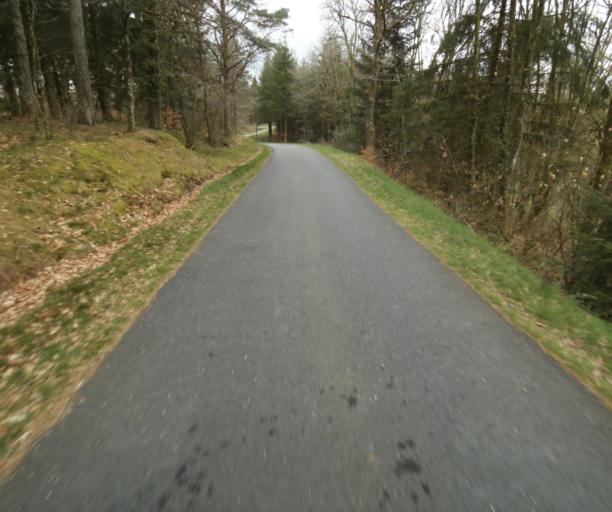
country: FR
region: Limousin
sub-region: Departement de la Correze
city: Correze
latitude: 45.3050
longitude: 1.9079
